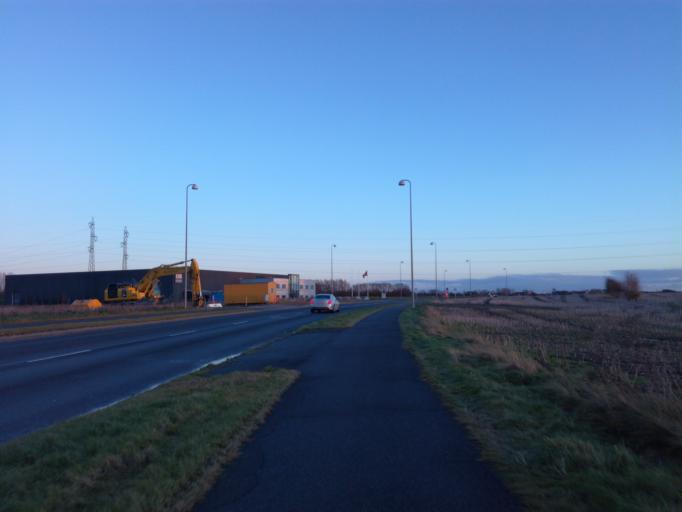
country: DK
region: South Denmark
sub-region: Fredericia Kommune
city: Taulov
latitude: 55.5552
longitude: 9.6587
